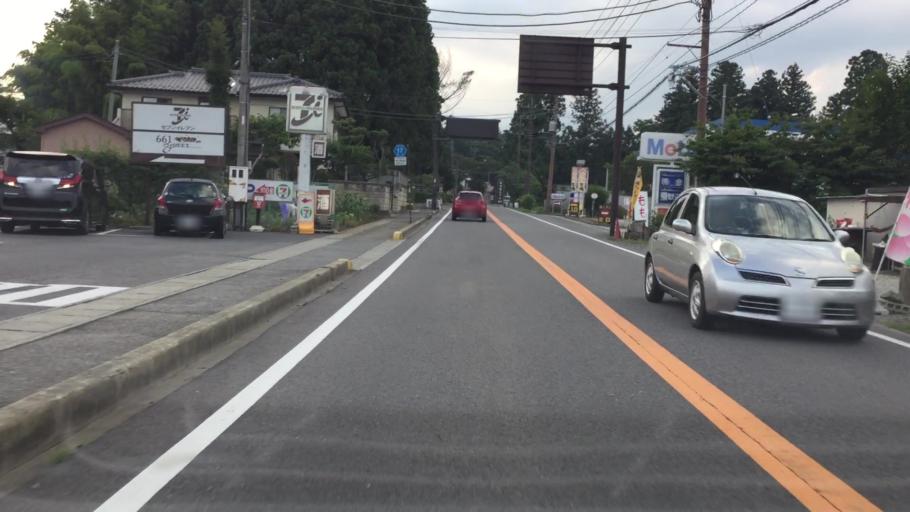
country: JP
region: Tochigi
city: Kuroiso
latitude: 37.0080
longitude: 140.0320
